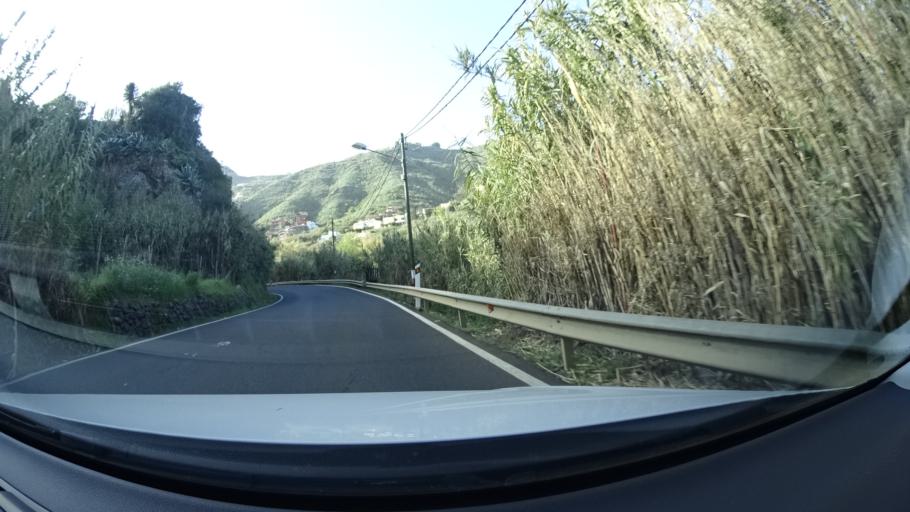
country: ES
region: Canary Islands
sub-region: Provincia de Las Palmas
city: Vega de San Mateo
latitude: 28.0169
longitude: -15.5547
